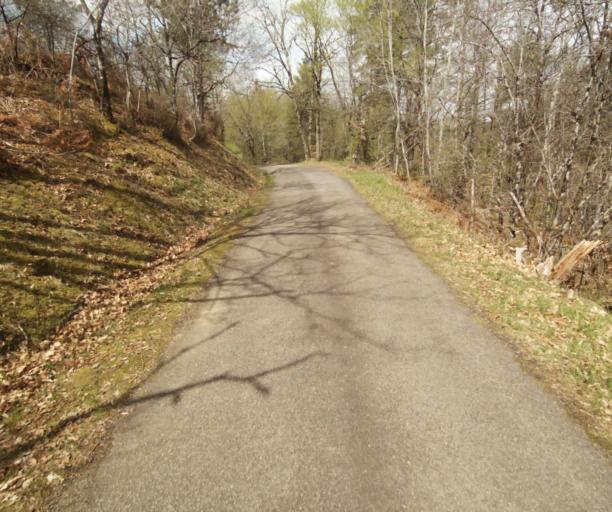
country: FR
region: Limousin
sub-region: Departement de la Correze
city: Sainte-Fortunade
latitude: 45.1875
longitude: 1.8669
